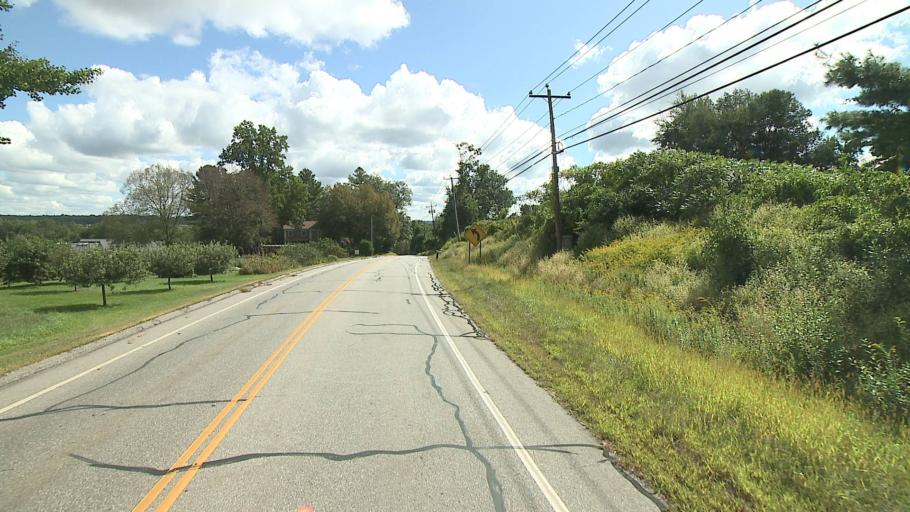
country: US
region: Connecticut
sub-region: Windham County
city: South Woodstock
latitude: 41.8968
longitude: -71.9486
